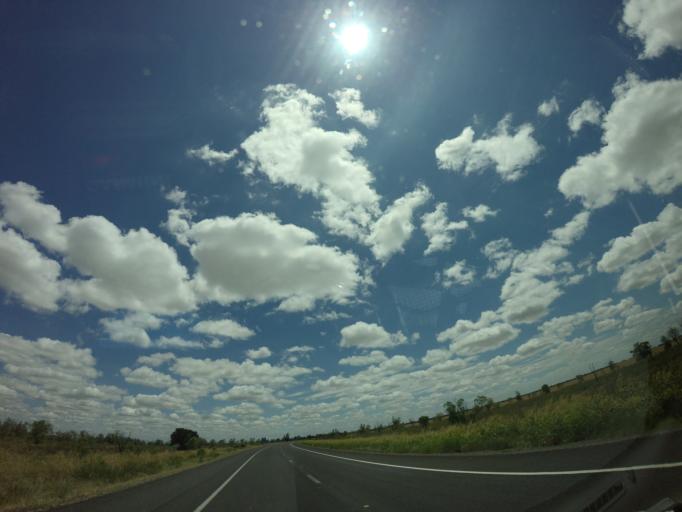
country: AU
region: New South Wales
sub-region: Moree Plains
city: Moree
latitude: -29.0453
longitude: 150.0482
